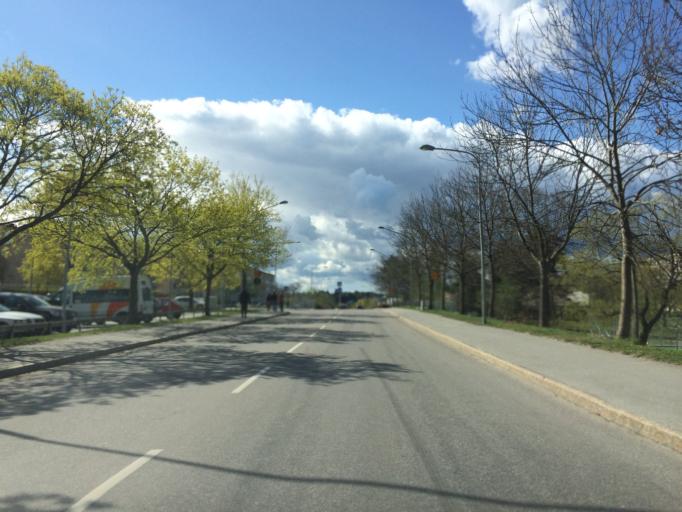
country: SE
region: Stockholm
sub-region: Huddinge Kommun
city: Segeltorp
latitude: 59.2935
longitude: 17.9326
